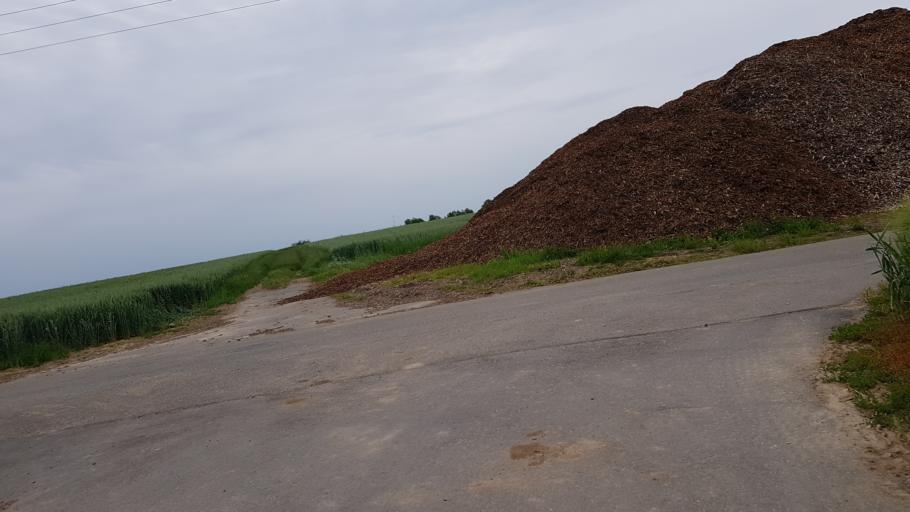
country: DE
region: Baden-Wuerttemberg
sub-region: Regierungsbezirk Stuttgart
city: Steinheim am der Murr
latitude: 48.9562
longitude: 9.2840
